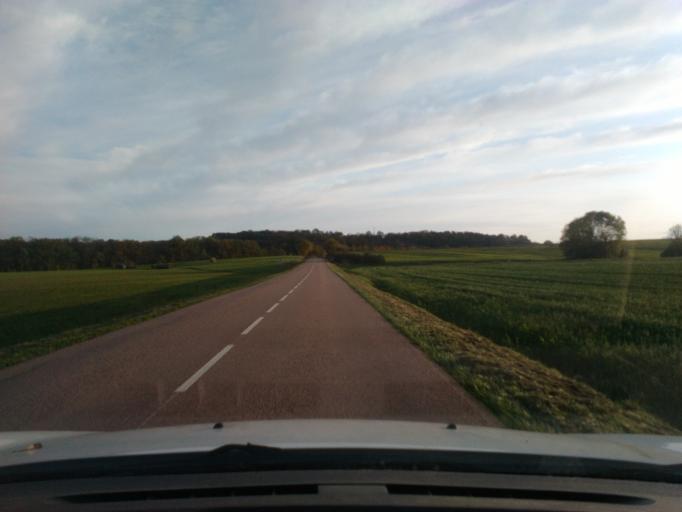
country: FR
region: Lorraine
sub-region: Departement des Vosges
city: Mirecourt
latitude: 48.2219
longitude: 6.1553
